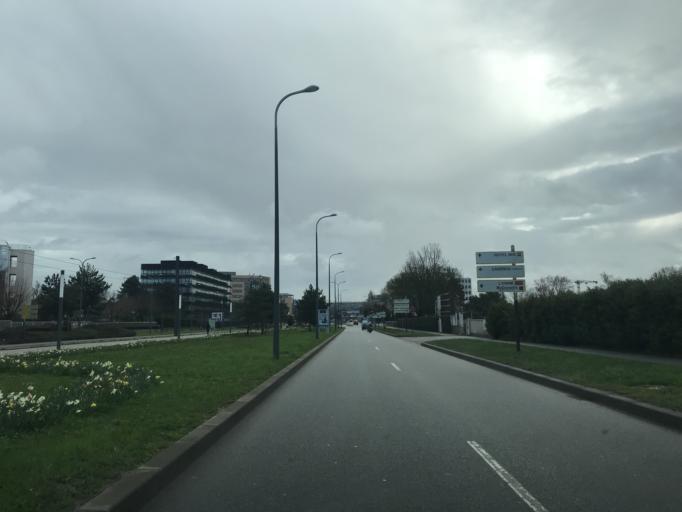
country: FR
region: Ile-de-France
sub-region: Departement des Yvelines
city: Velizy-Villacoublay
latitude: 48.7820
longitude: 2.2112
